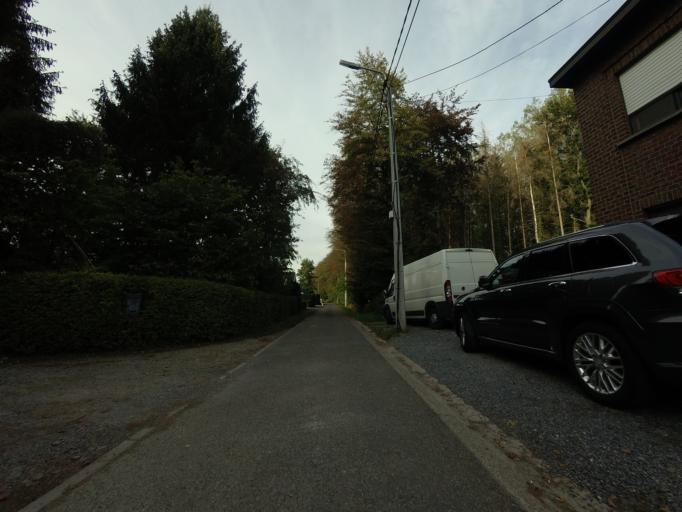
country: BE
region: Flanders
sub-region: Provincie Vlaams-Brabant
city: Kortenberg
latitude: 50.8952
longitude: 4.5918
